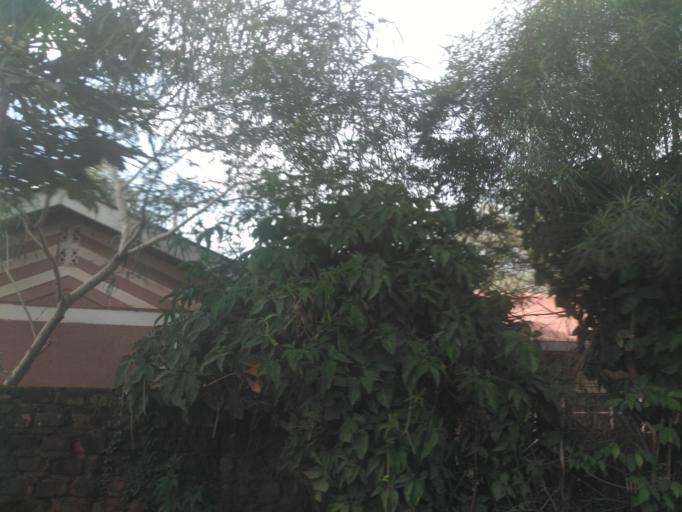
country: UG
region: Central Region
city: Kampala Central Division
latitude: 0.3583
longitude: 32.5806
